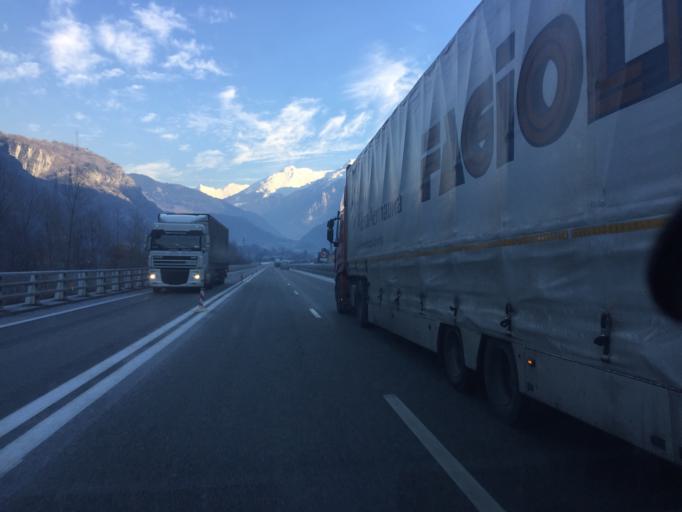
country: FR
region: Rhone-Alpes
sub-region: Departement de la Savoie
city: Val Thorens
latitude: 45.2061
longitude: 6.5745
